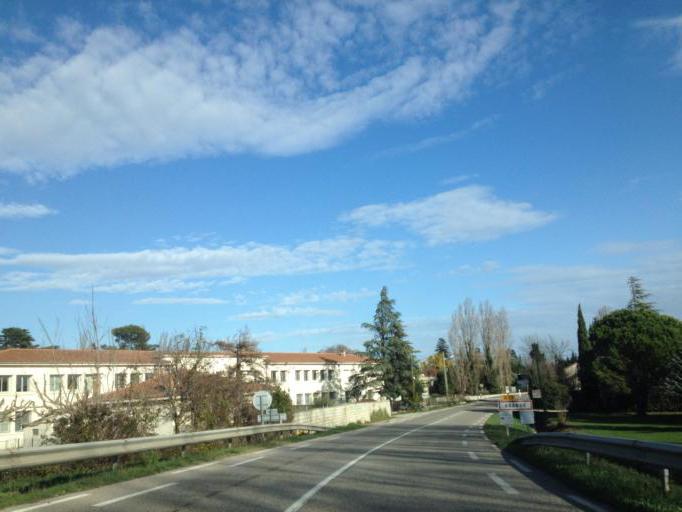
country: FR
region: Provence-Alpes-Cote d'Azur
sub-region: Departement du Vaucluse
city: Orange
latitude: 44.1359
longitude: 4.7860
